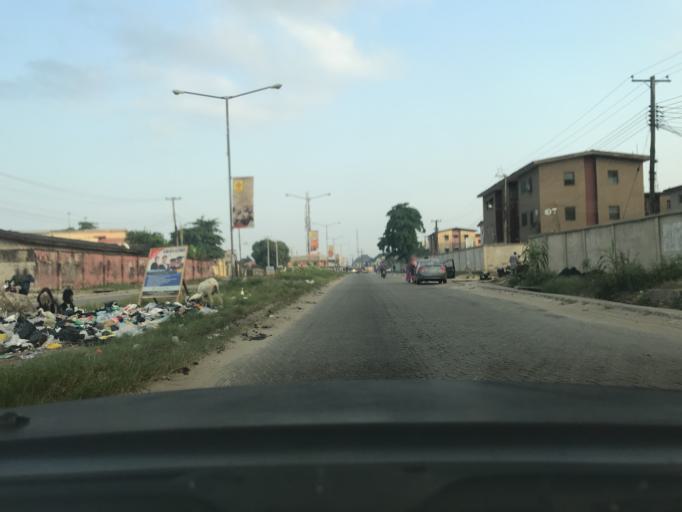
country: NG
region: Lagos
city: Ajegunle
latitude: 6.4632
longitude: 3.3091
